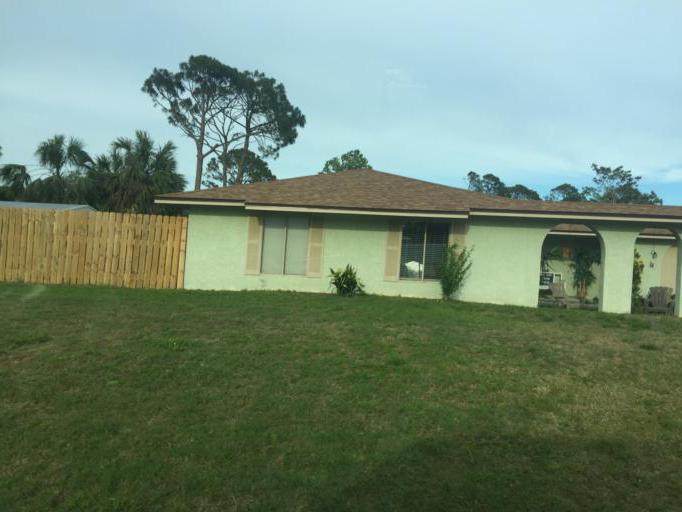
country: US
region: Florida
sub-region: Bay County
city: Lower Grand Lagoon
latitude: 30.1660
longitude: -85.7708
